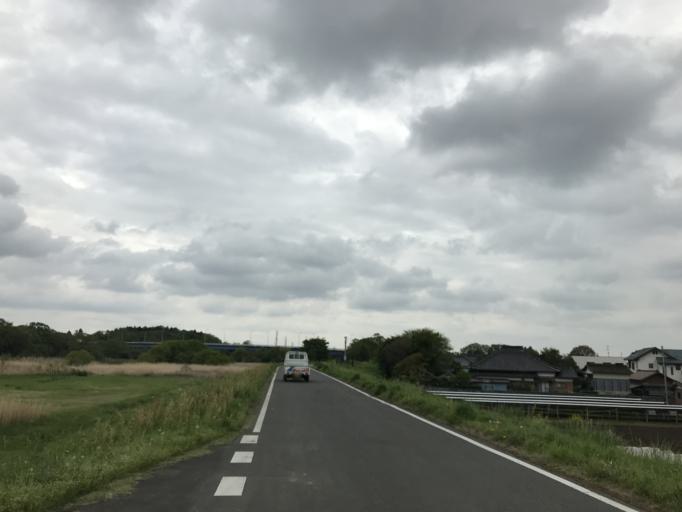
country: JP
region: Ibaraki
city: Mitsukaido
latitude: 36.0424
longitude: 140.0242
